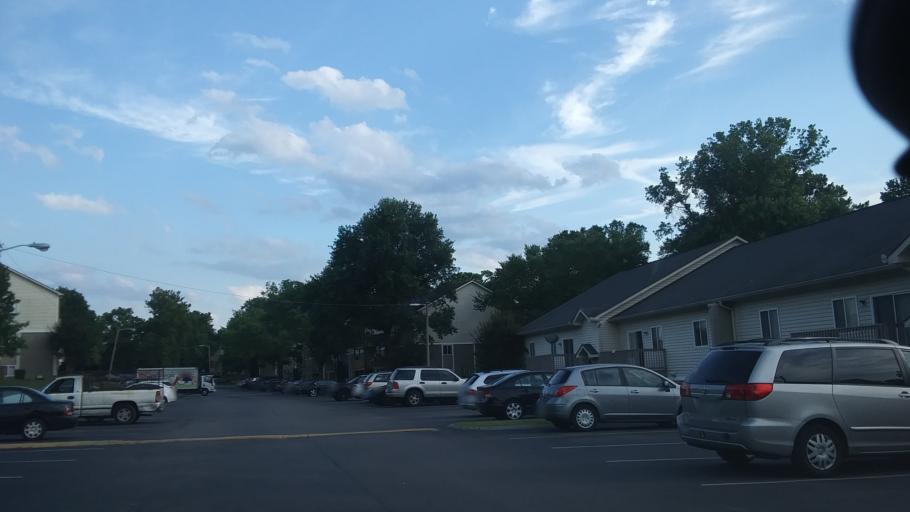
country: US
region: Tennessee
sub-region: Davidson County
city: Oak Hill
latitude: 36.0834
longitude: -86.7162
